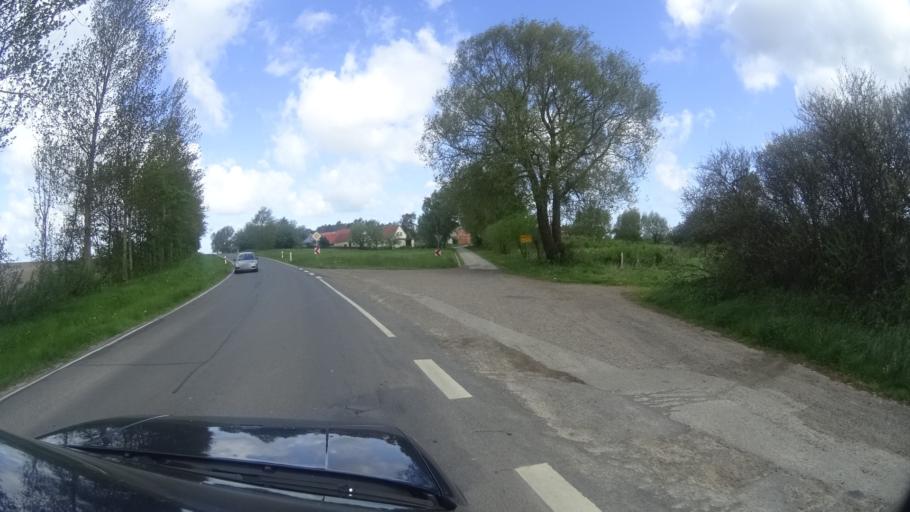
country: DE
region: Mecklenburg-Vorpommern
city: Trinwillershagen
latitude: 54.3179
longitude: 12.5823
